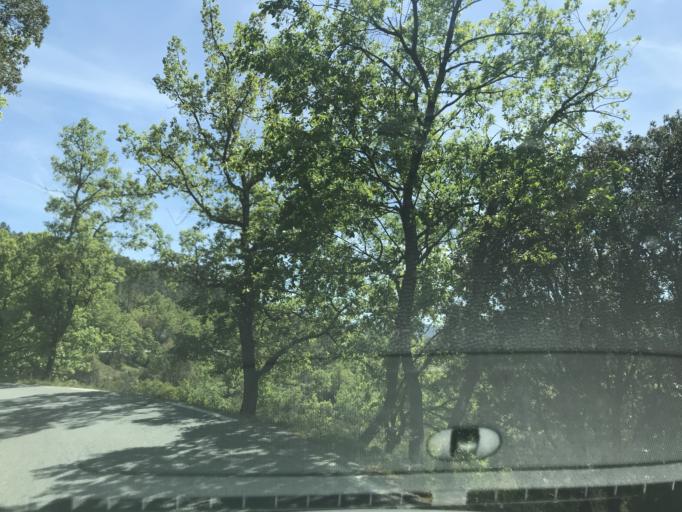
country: FR
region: Provence-Alpes-Cote d'Azur
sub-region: Departement du Var
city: Montauroux
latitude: 43.5851
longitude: 6.8159
